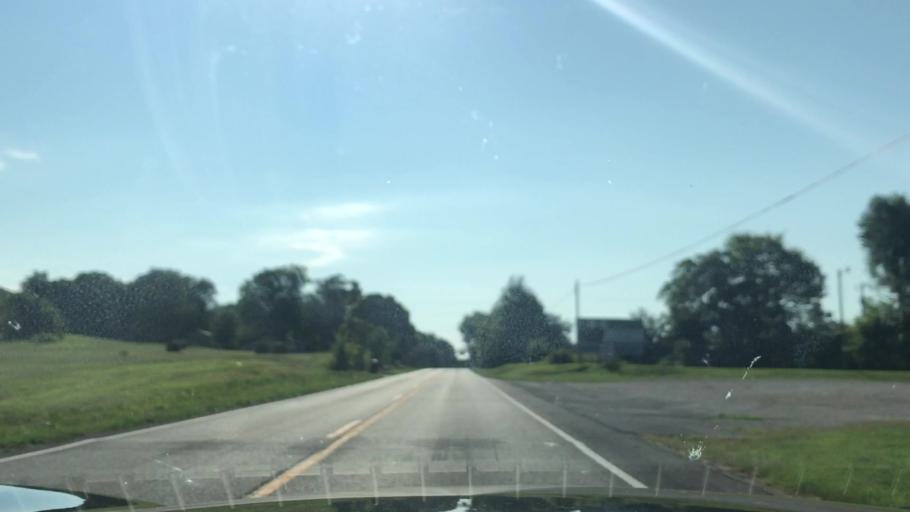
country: US
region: Kentucky
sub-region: Hart County
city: Horse Cave
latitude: 37.1763
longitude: -85.8715
